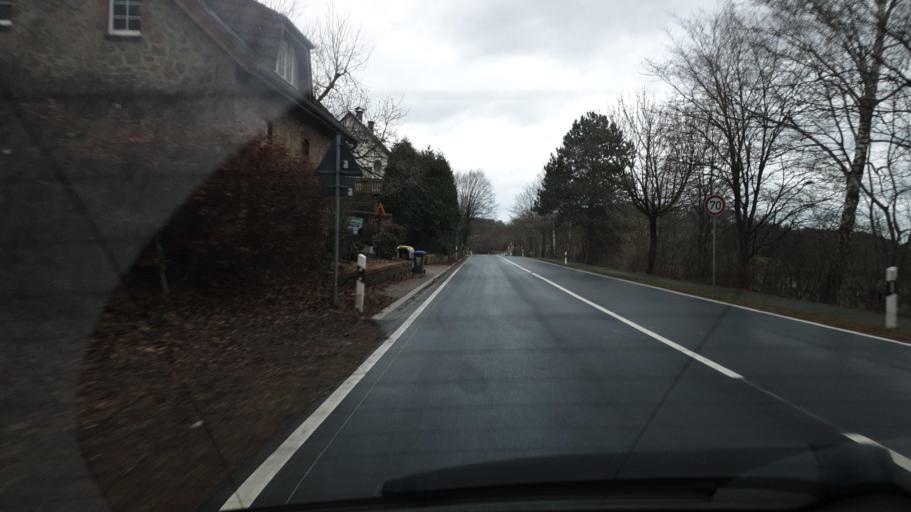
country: DE
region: North Rhine-Westphalia
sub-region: Regierungsbezirk Detmold
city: Vlotho
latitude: 52.1241
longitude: 8.8546
